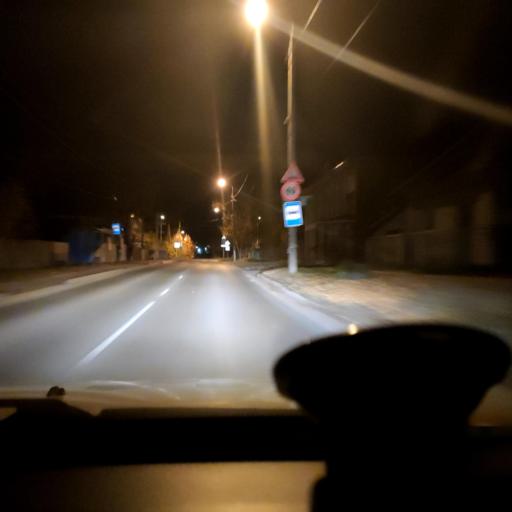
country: RU
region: Perm
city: Perm
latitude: 58.0212
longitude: 56.3141
